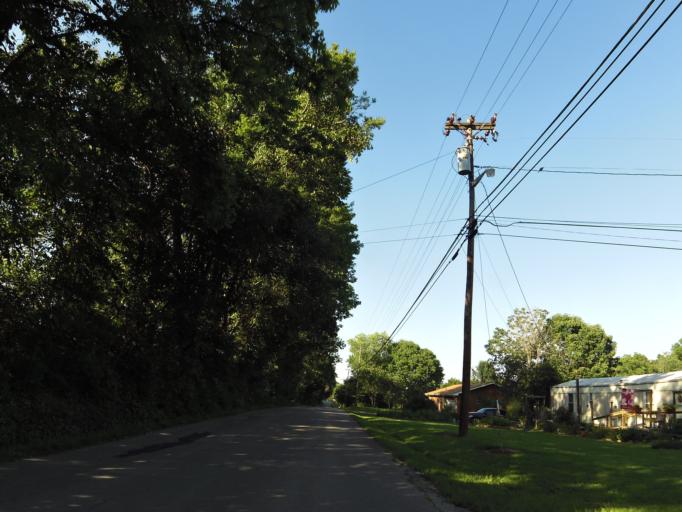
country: US
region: Tennessee
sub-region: Blount County
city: Wildwood
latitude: 35.7443
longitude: -83.8798
